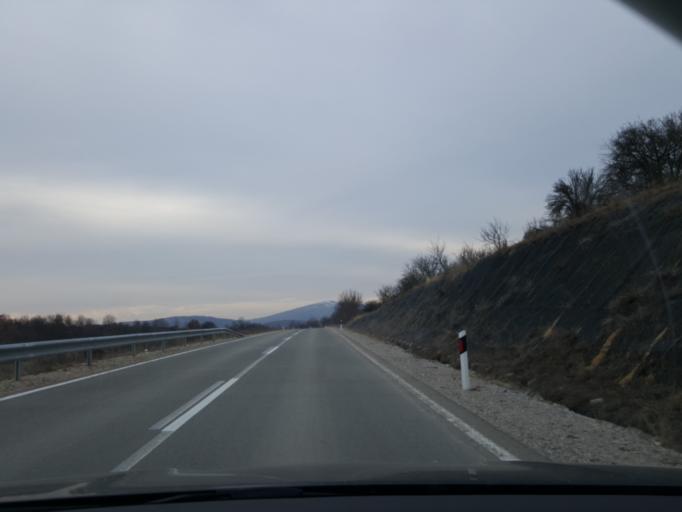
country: RS
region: Central Serbia
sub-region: Pirotski Okrug
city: Bela Palanka
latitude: 43.2309
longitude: 22.4242
